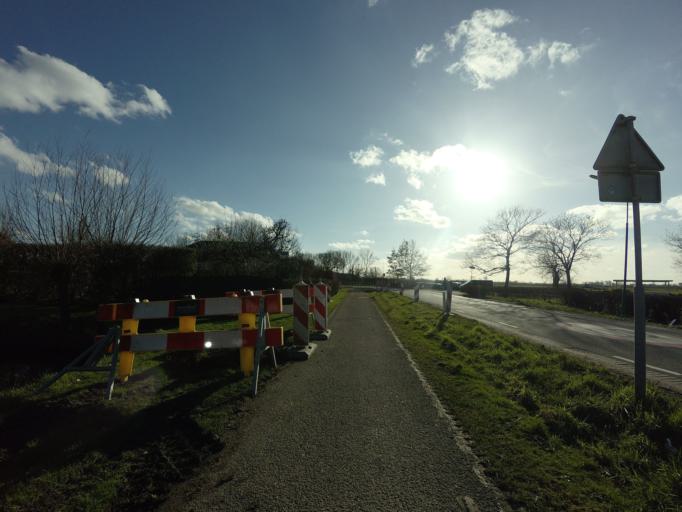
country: NL
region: Utrecht
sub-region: Gemeente IJsselstein
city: IJsselstein
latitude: 52.0011
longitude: 5.0491
